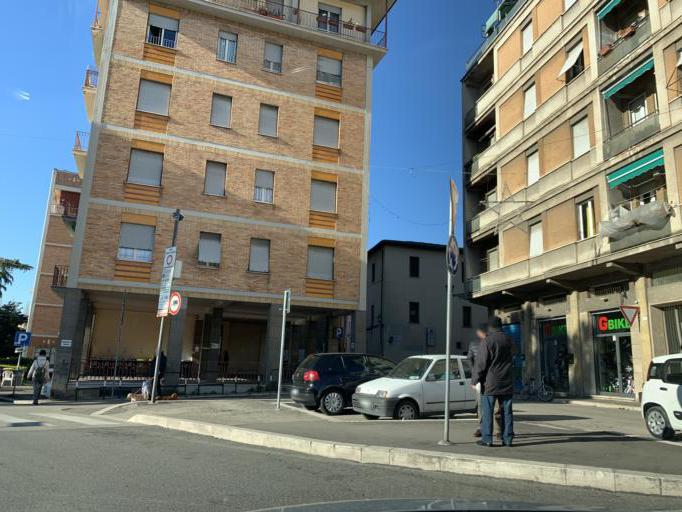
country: IT
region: Umbria
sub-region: Provincia di Terni
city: Terni
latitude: 42.5611
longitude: 12.6507
